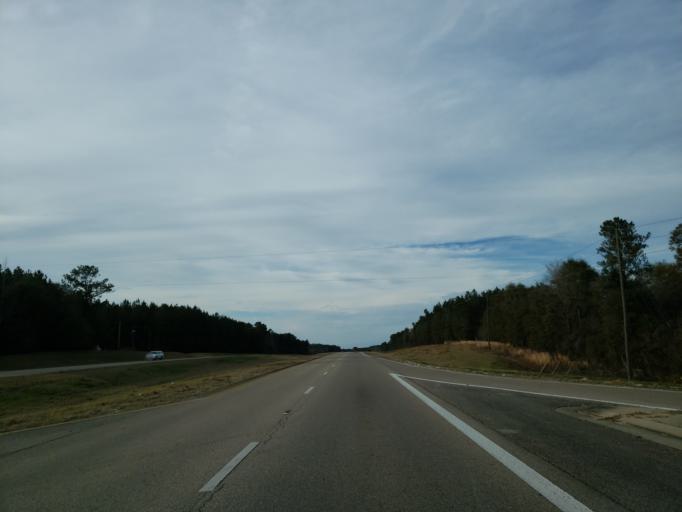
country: US
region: Mississippi
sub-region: Wayne County
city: Waynesboro
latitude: 31.6186
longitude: -88.5782
